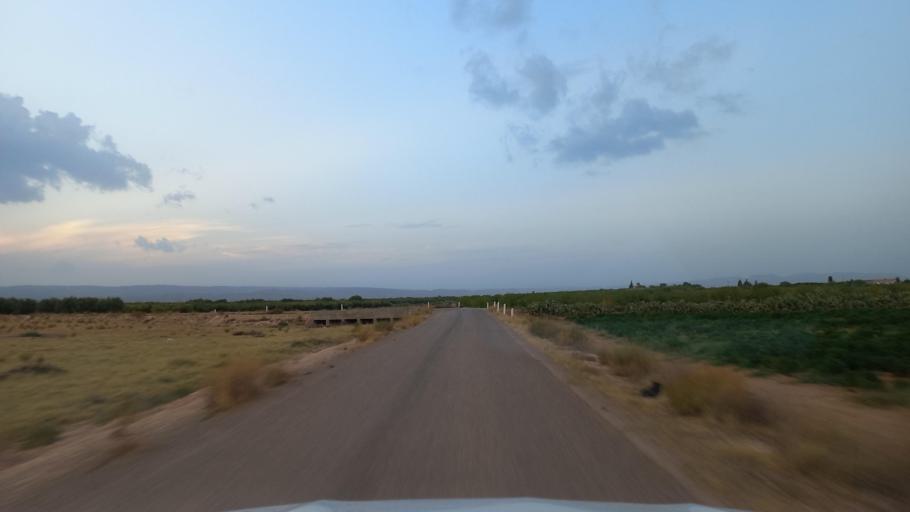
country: TN
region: Al Qasrayn
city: Kasserine
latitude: 35.2740
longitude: 9.0438
